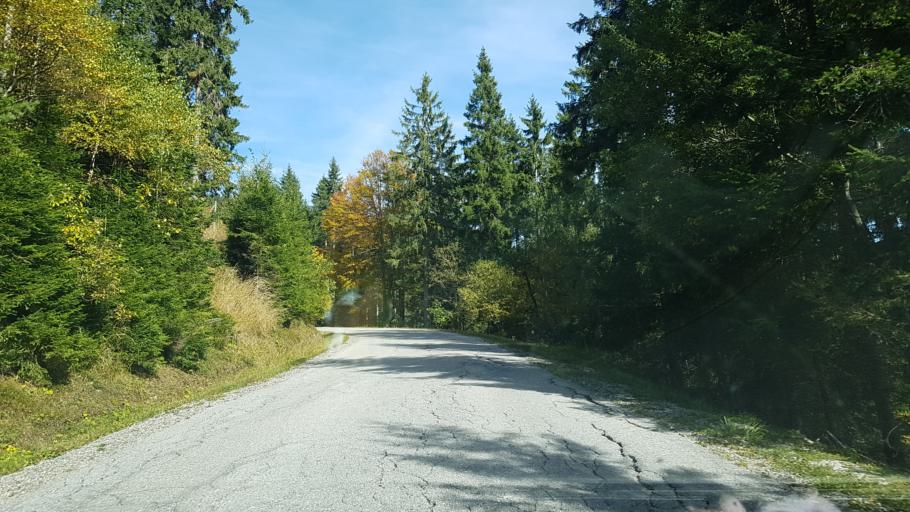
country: SI
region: Slovenj Gradec
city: Legen
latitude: 46.4990
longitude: 15.2002
